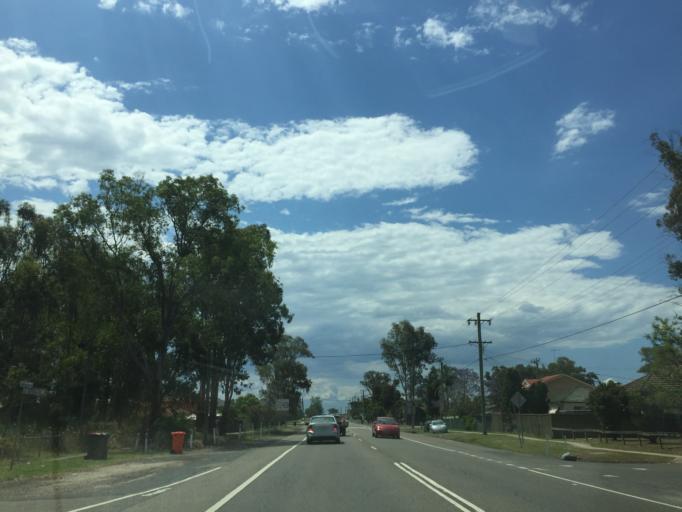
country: AU
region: New South Wales
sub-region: Blacktown
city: Glendenning
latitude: -33.7490
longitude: 150.8417
